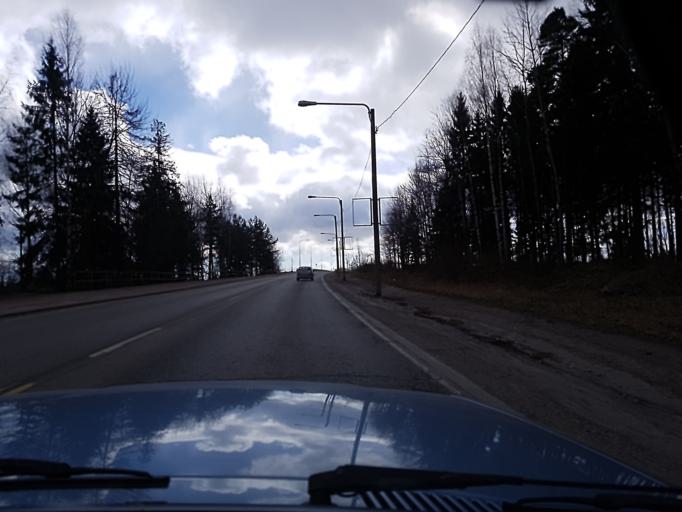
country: FI
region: Uusimaa
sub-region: Helsinki
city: Helsinki
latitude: 60.2197
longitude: 24.9334
